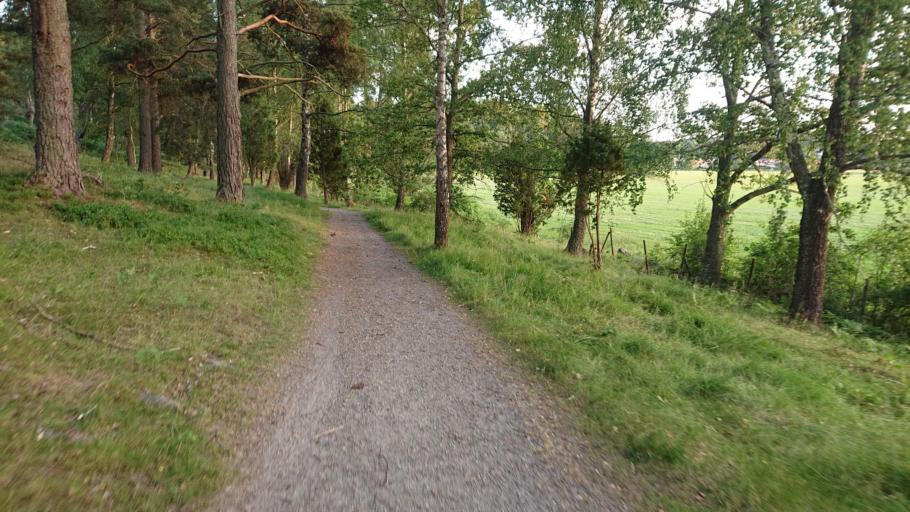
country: SE
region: Stockholm
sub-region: Osterakers Kommun
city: Akersberga
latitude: 59.4955
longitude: 18.2971
